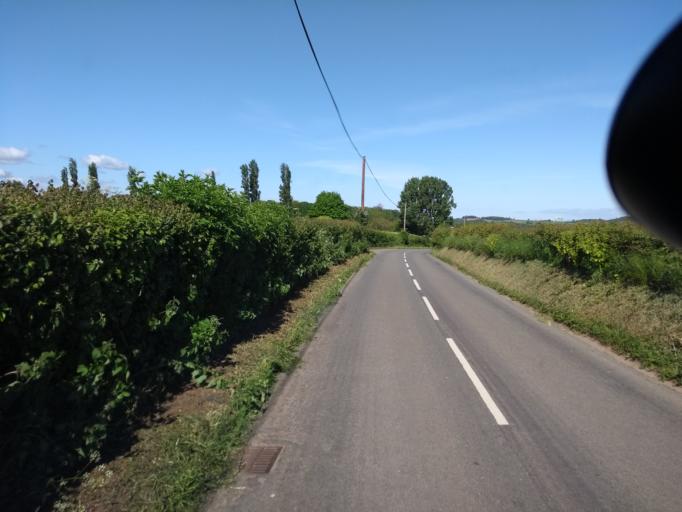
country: GB
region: England
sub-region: Somerset
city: Bridgwater
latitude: 51.1367
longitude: -3.0409
